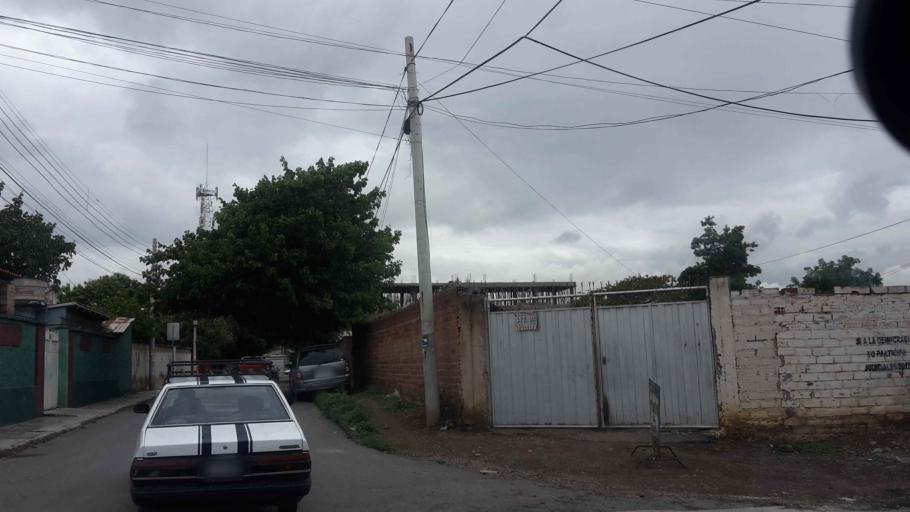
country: BO
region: Cochabamba
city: Cochabamba
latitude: -17.3616
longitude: -66.1790
